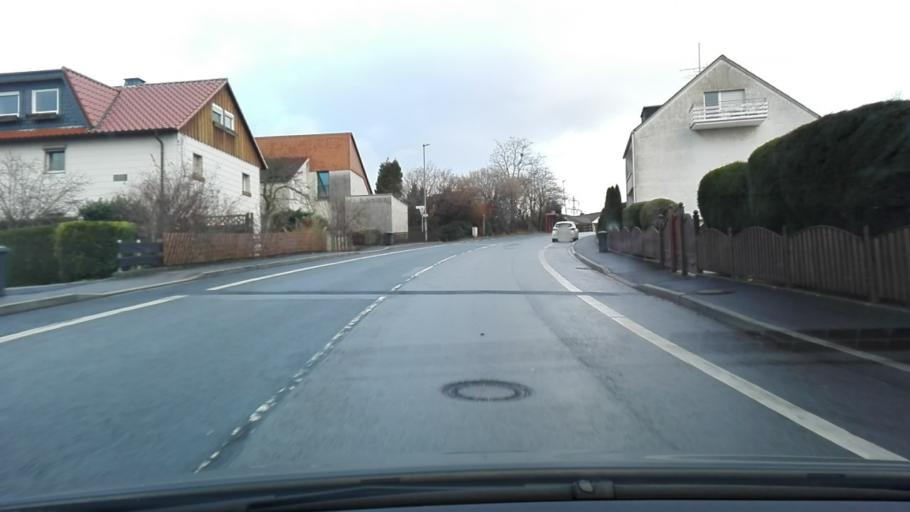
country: DE
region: North Rhine-Westphalia
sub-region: Regierungsbezirk Arnsberg
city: Frondenberg
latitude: 51.4819
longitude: 7.7832
